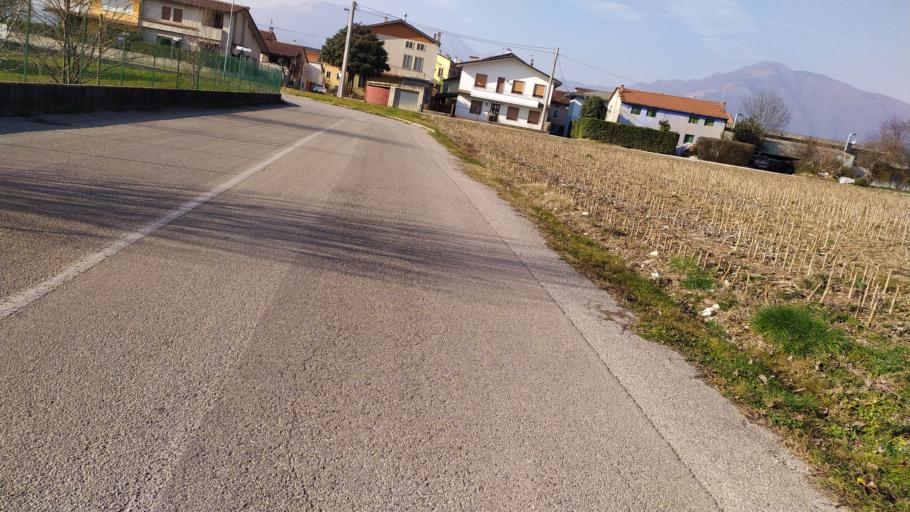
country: IT
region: Veneto
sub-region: Provincia di Vicenza
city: Giavenale
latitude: 45.6881
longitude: 11.4012
